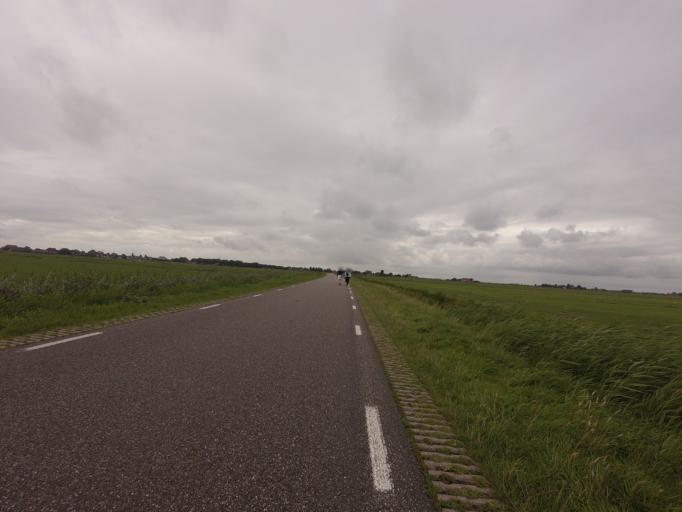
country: NL
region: Friesland
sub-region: Sudwest Fryslan
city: Heeg
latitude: 52.9691
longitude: 5.5560
